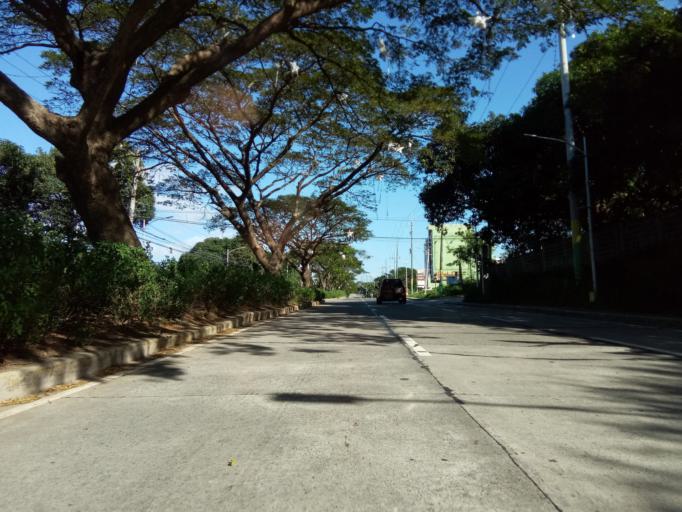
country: PH
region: Calabarzon
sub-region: Province of Cavite
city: Dasmarinas
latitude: 14.3505
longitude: 120.9628
